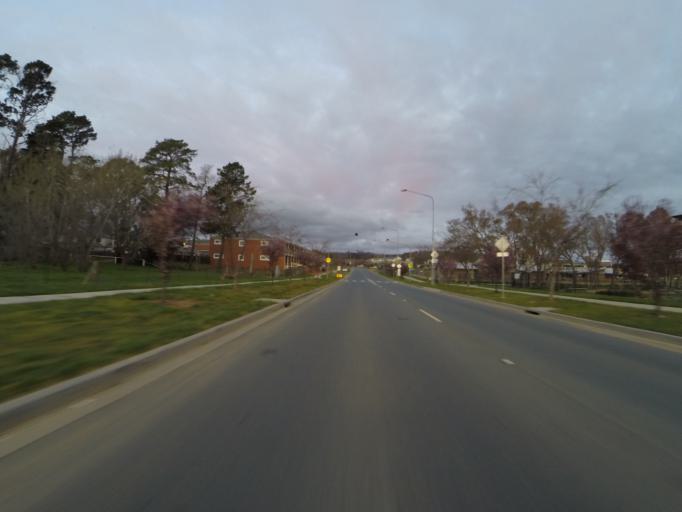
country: AU
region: Australian Capital Territory
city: Kaleen
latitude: -35.1944
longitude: 149.1542
